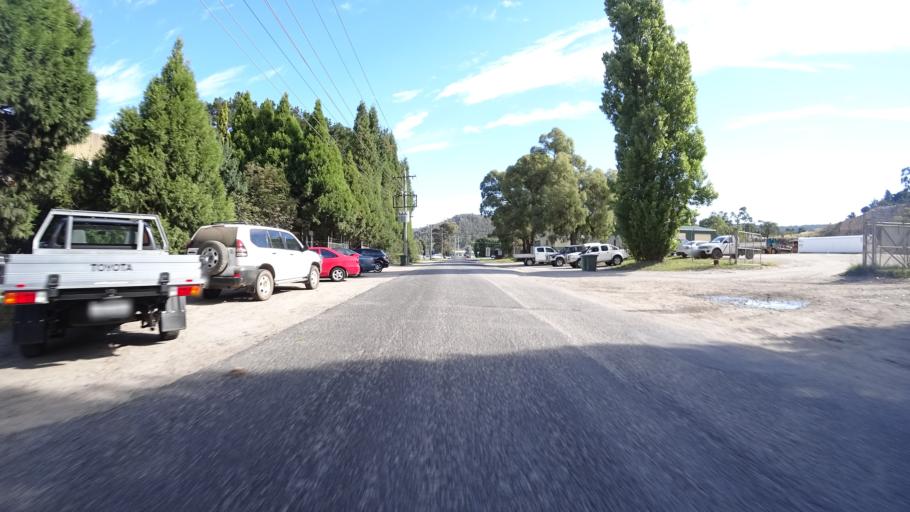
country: AU
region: New South Wales
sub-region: Lithgow
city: Lithgow
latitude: -33.4783
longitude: 150.1746
